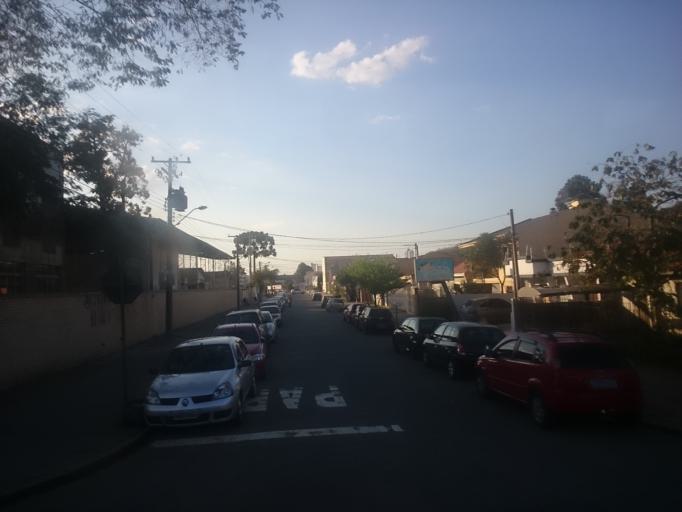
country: BR
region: Parana
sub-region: Curitiba
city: Curitiba
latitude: -25.4503
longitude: -49.2564
